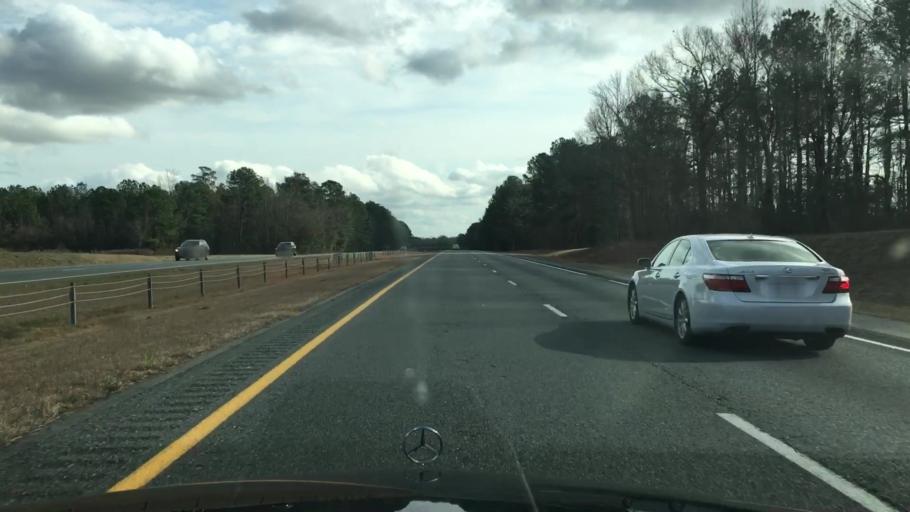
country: US
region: North Carolina
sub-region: Sampson County
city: Clinton
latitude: 35.2192
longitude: -78.3349
